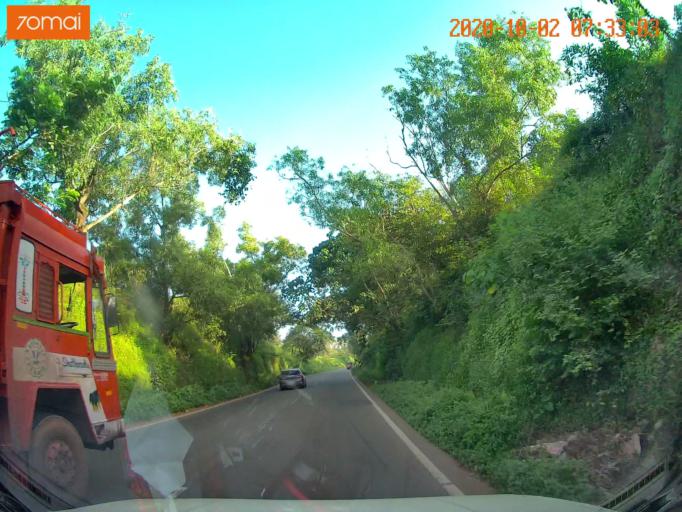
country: IN
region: Kerala
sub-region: Malappuram
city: Pariyapuram
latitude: 11.0561
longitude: 75.9356
